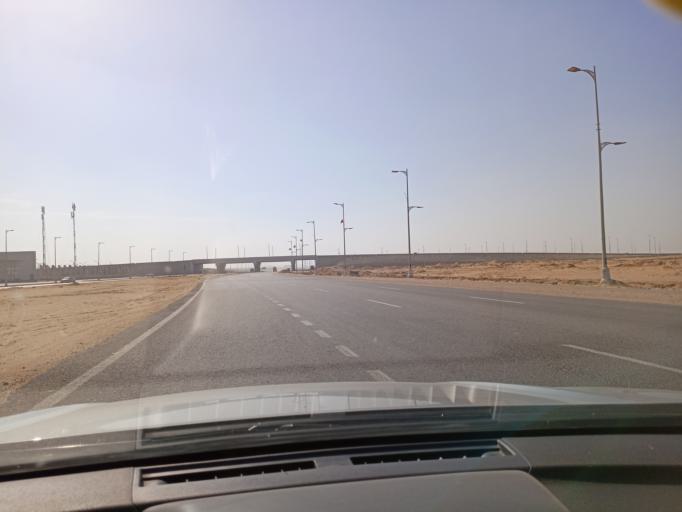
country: EG
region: Muhafazat al Qalyubiyah
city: Al Khankah
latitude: 30.0443
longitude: 31.6901
